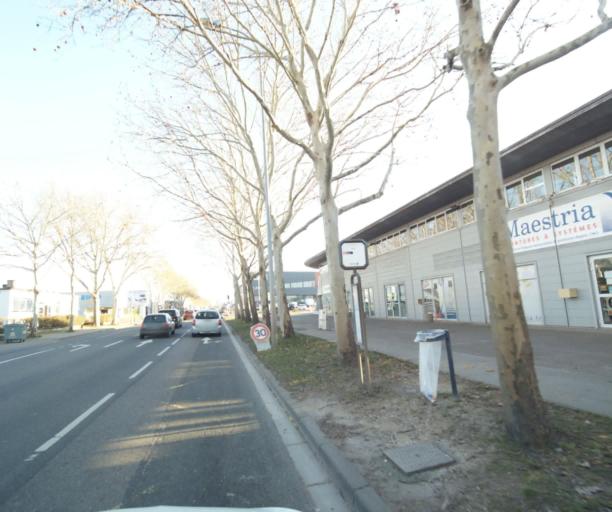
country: FR
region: Lorraine
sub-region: Departement de Meurthe-et-Moselle
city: Tomblaine
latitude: 48.6828
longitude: 6.2030
